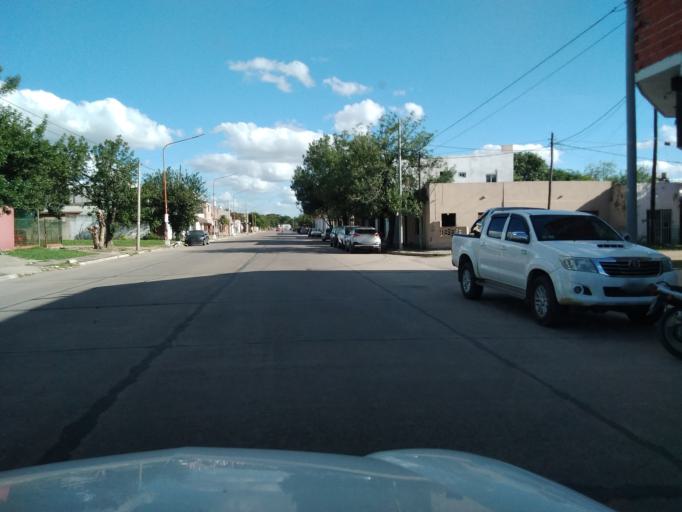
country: AR
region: Corrientes
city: Corrientes
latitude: -27.4943
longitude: -58.8338
